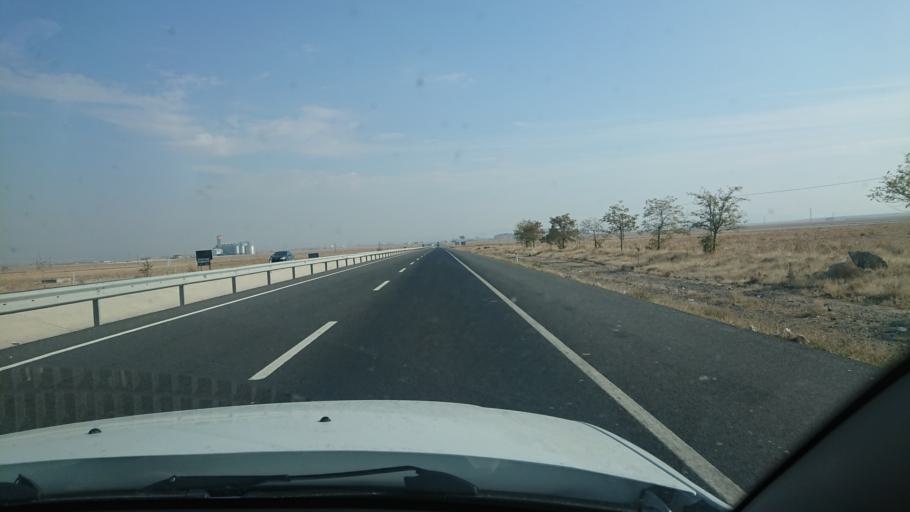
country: TR
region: Aksaray
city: Yesilova
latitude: 38.3282
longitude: 33.8969
